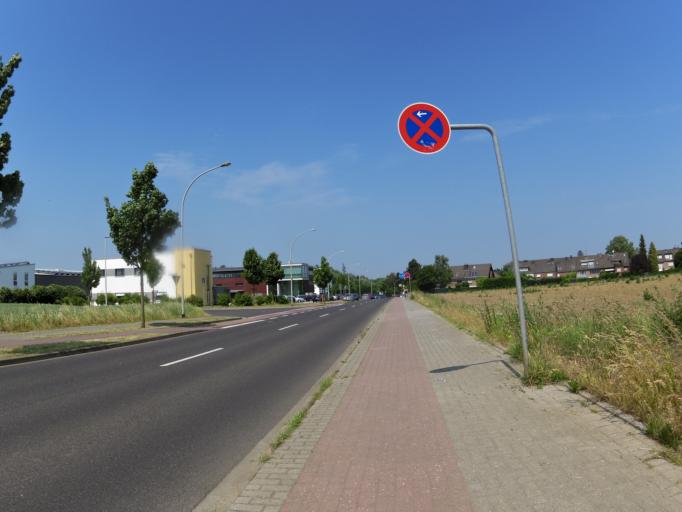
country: DE
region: North Rhine-Westphalia
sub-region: Regierungsbezirk Koln
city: Aachen
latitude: 50.8223
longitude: 6.0830
